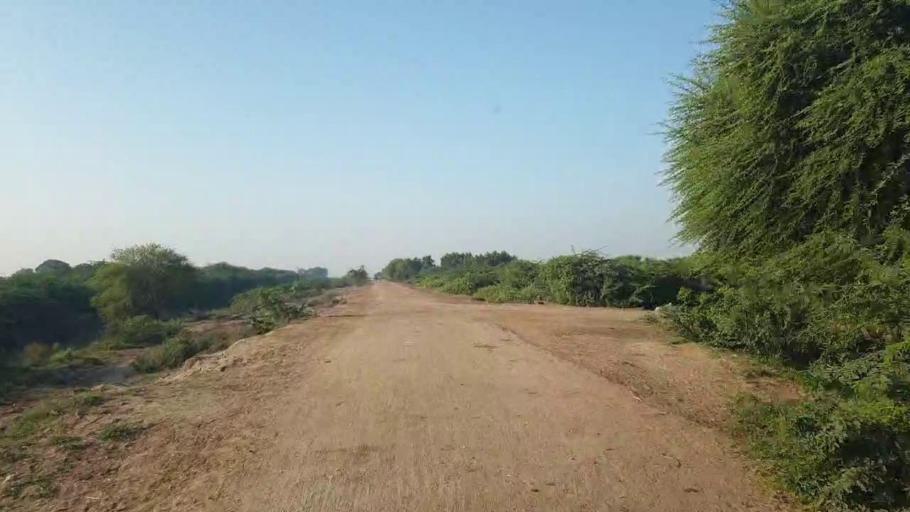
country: PK
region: Sindh
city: Badin
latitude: 24.5998
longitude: 68.7755
